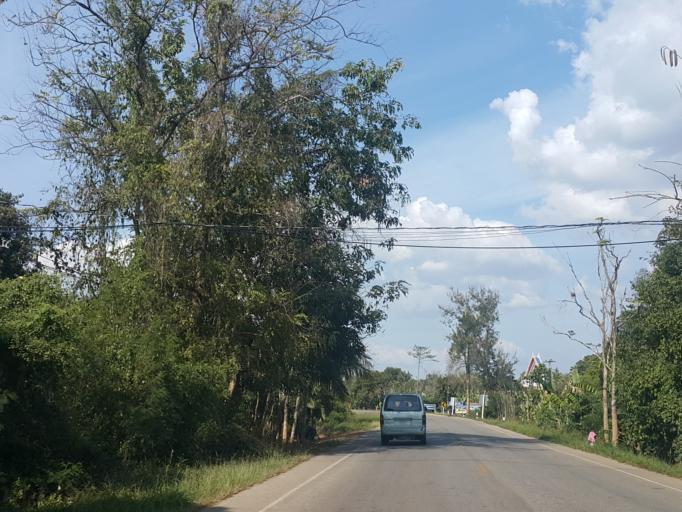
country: TH
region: Sukhothai
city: Sawankhalok
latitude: 17.2613
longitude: 99.8361
